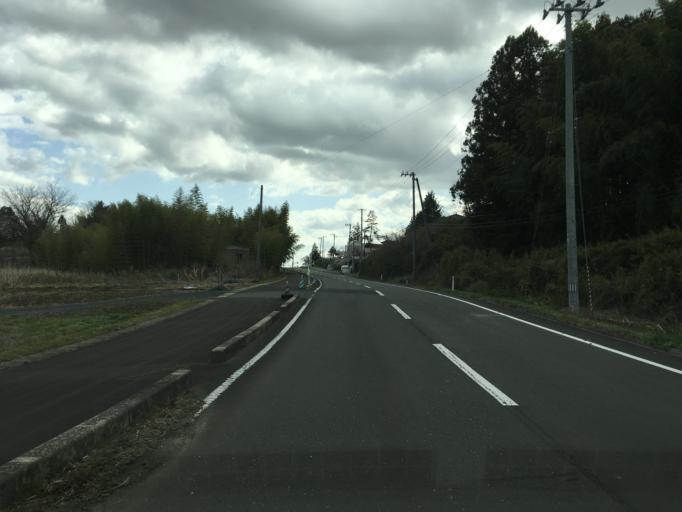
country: JP
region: Iwate
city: Ichinoseki
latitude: 38.7526
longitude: 141.2676
